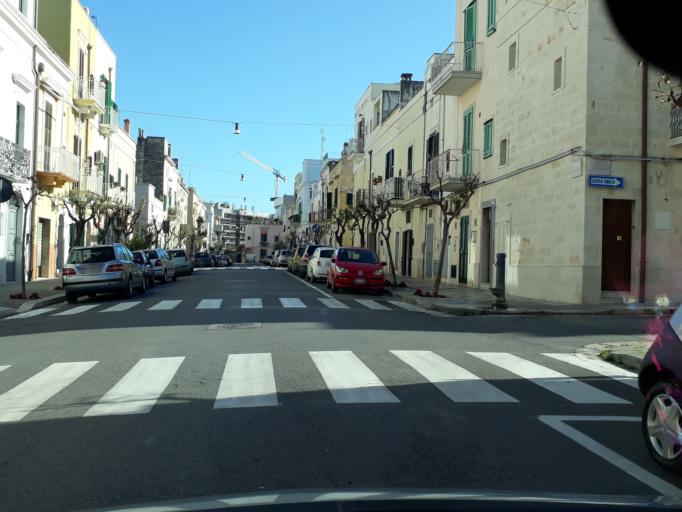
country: IT
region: Apulia
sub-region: Provincia di Bari
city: Monopoli
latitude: 40.9504
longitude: 17.2996
